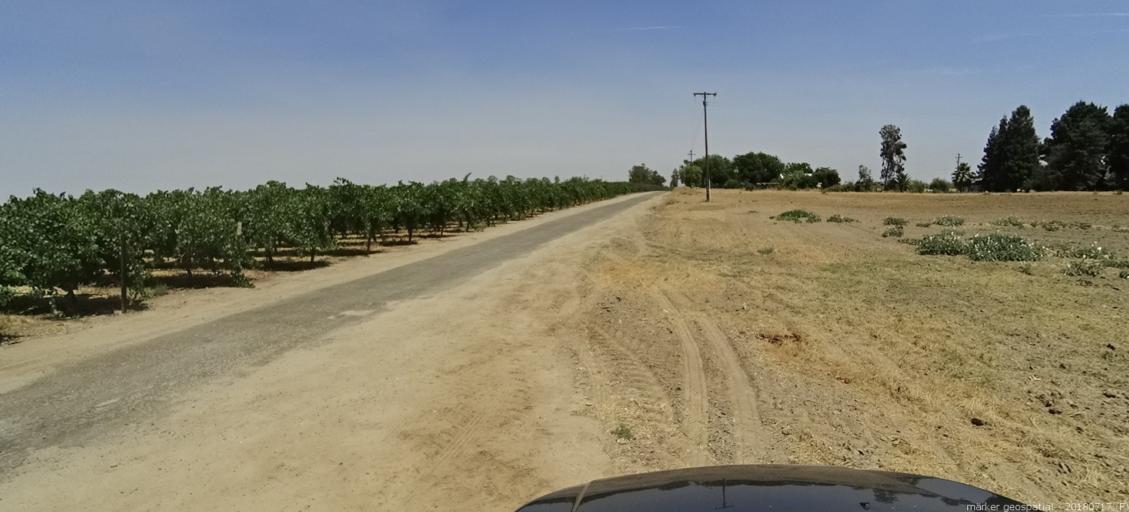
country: US
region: California
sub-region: Madera County
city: Madera Acres
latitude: 37.0545
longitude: -120.1152
